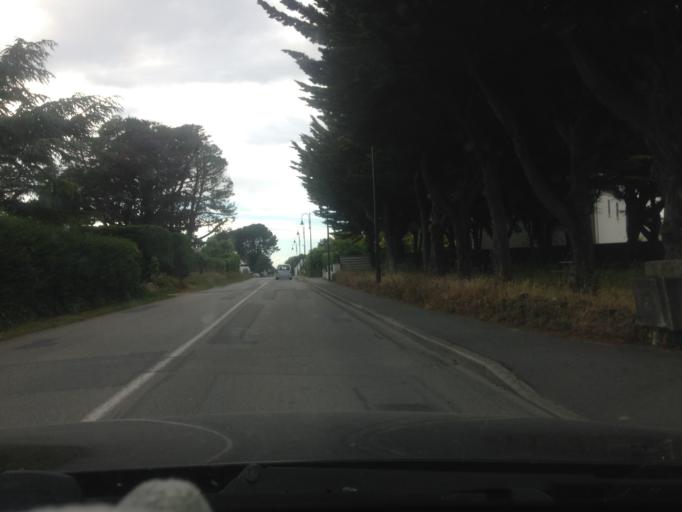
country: FR
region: Brittany
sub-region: Departement du Morbihan
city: Carnac
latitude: 47.5869
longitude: -3.0878
